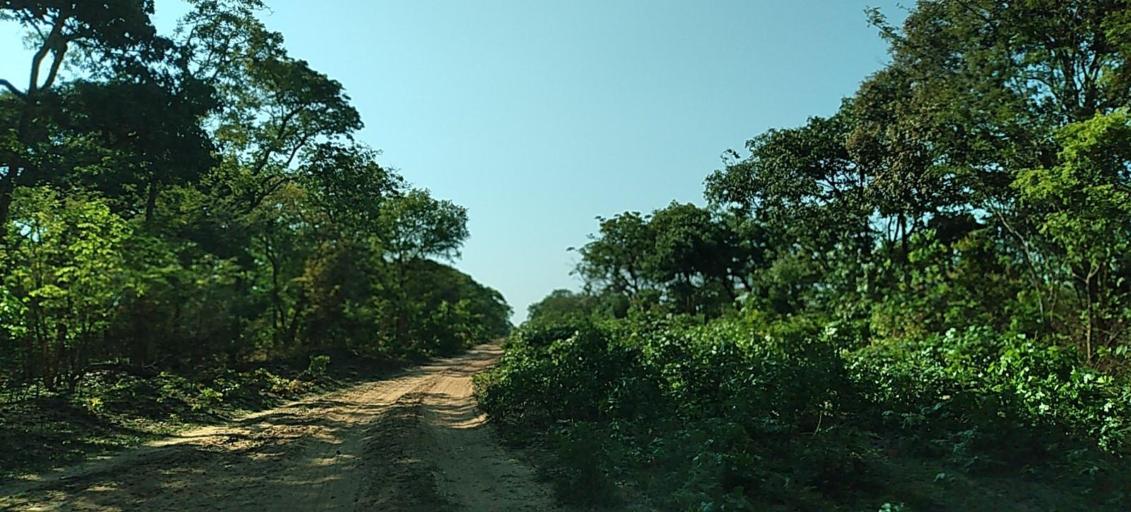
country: ZM
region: Central
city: Mkushi
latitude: -13.4729
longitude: 28.9188
